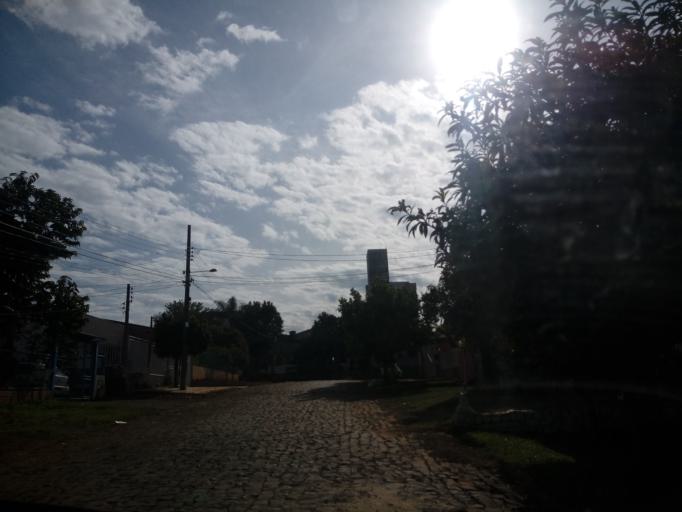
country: BR
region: Santa Catarina
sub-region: Chapeco
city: Chapeco
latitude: -27.1207
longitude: -52.6304
